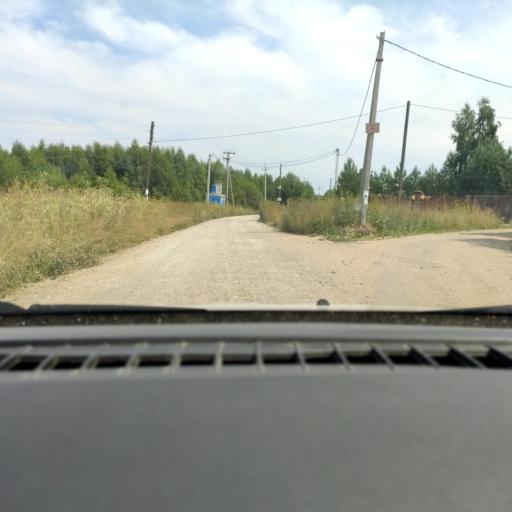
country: RU
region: Perm
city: Polazna
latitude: 58.1785
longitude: 56.4229
